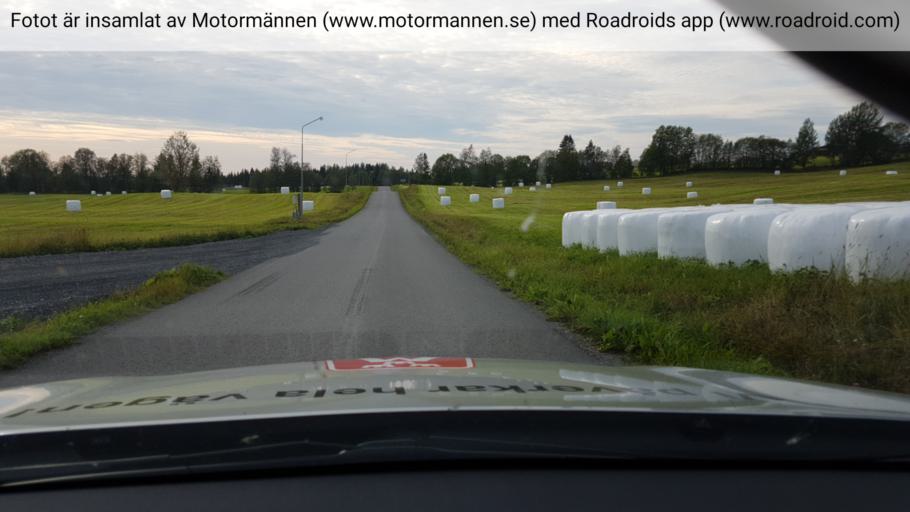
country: SE
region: Jaemtland
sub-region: OEstersunds Kommun
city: Lit
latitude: 63.5653
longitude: 14.9250
